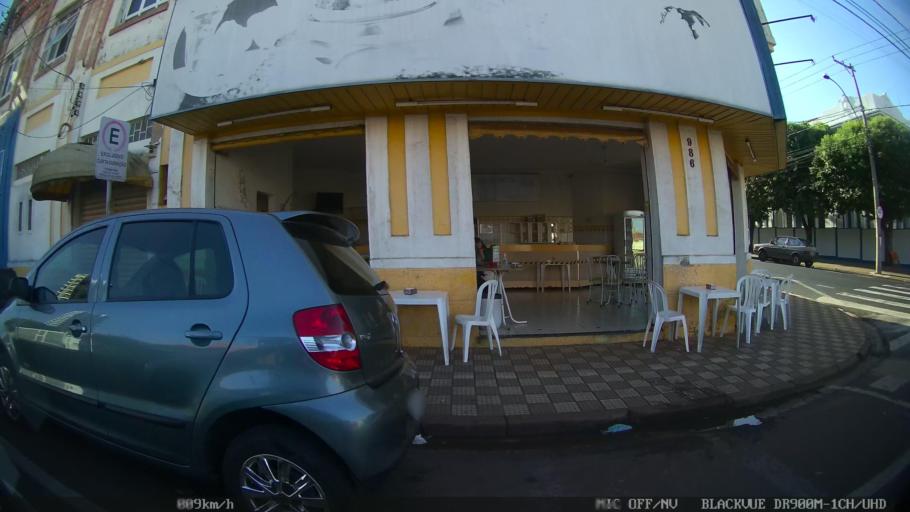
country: BR
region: Sao Paulo
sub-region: Sao Jose Do Rio Preto
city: Sao Jose do Rio Preto
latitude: -20.8076
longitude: -49.3862
